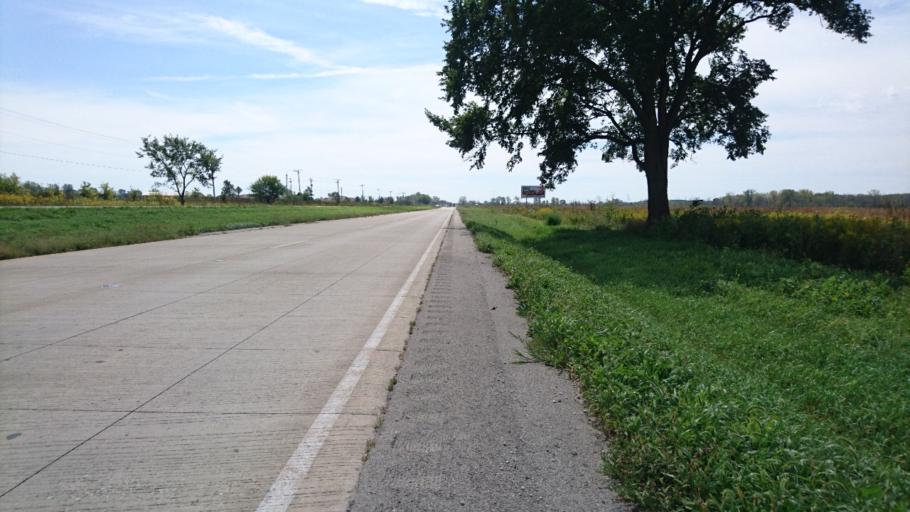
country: US
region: Illinois
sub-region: Will County
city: Wilmington
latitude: 41.3477
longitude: -88.1336
